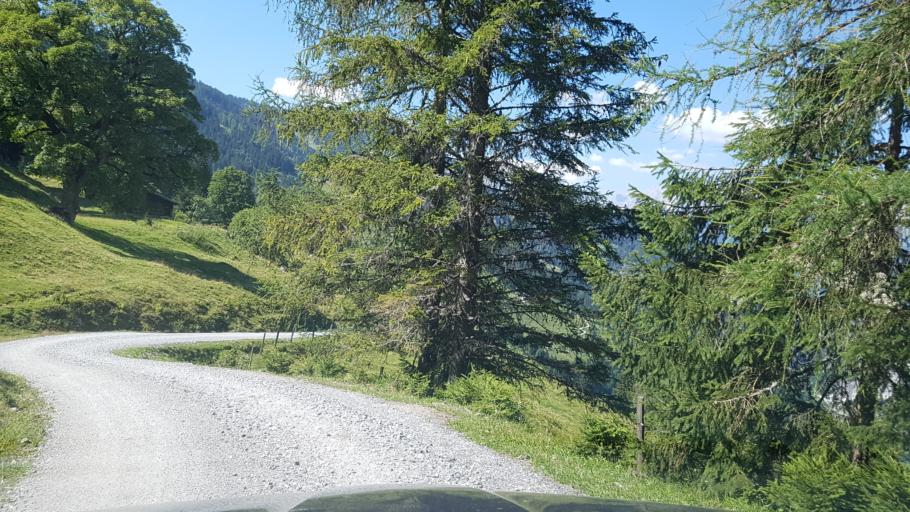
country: AT
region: Salzburg
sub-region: Politischer Bezirk Sankt Johann im Pongau
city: Dorfgastein
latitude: 47.2485
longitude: 13.0738
